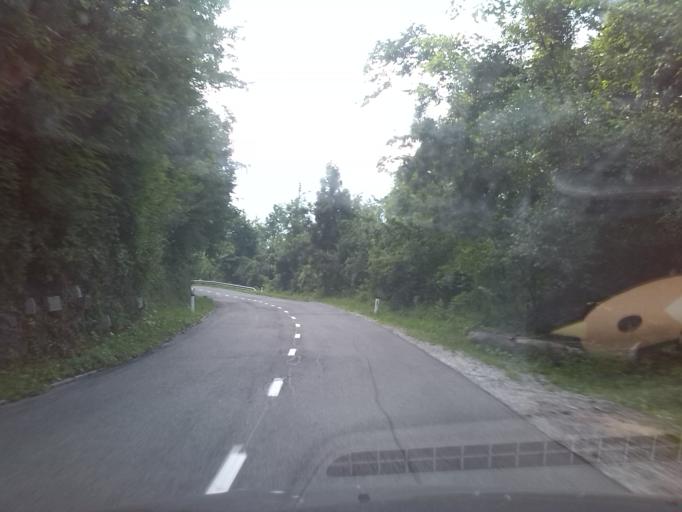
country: SI
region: Kobarid
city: Kobarid
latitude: 46.2116
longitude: 13.5973
